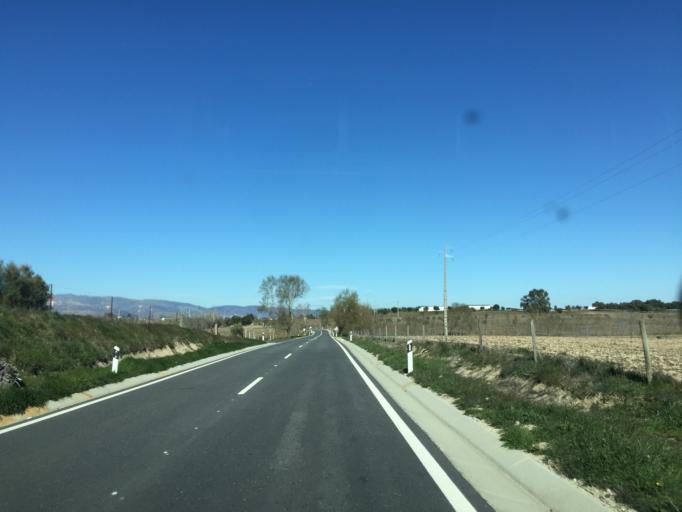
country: PT
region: Guarda
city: Alcains
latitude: 39.9622
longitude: -7.4538
